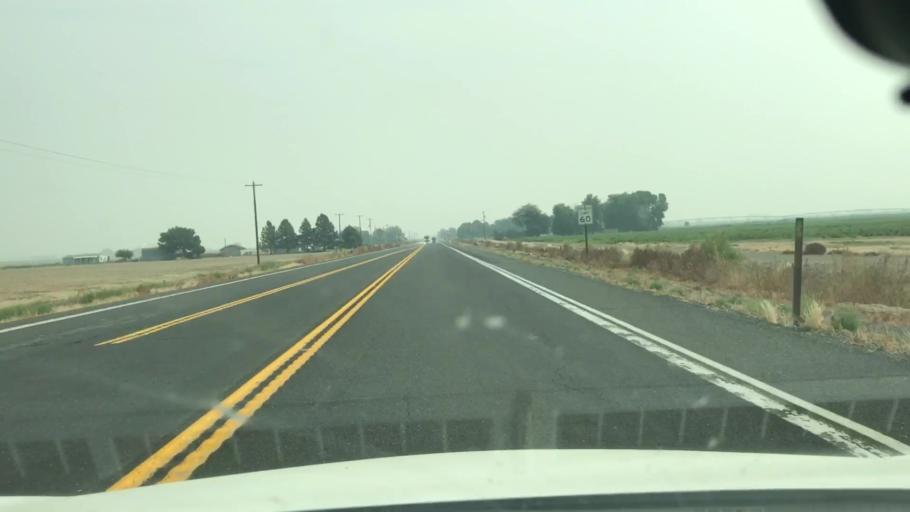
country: US
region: Washington
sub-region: Grant County
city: Quincy
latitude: 47.2343
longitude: -119.7667
